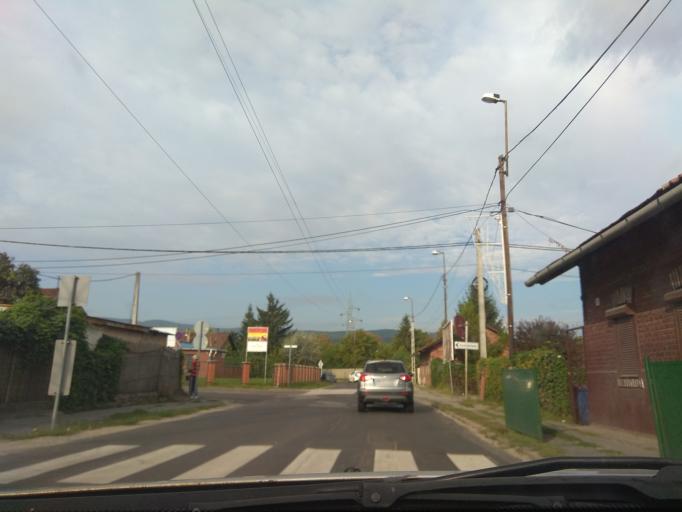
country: HU
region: Borsod-Abauj-Zemplen
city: Miskolc
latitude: 48.0891
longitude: 20.7264
